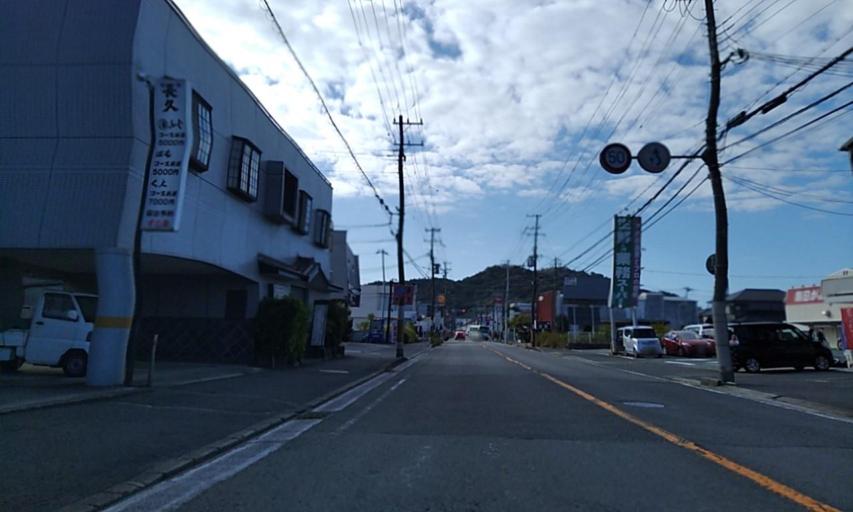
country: JP
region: Wakayama
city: Minato
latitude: 34.1997
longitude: 135.1590
